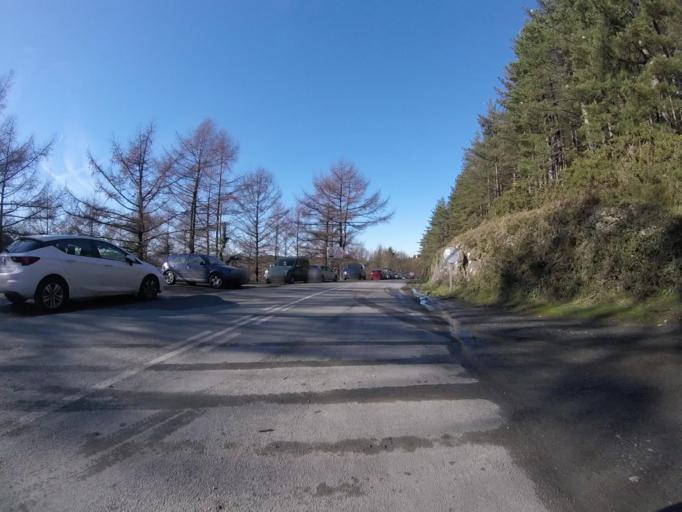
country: ES
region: Basque Country
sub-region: Provincia de Guipuzcoa
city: Irun
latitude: 43.2953
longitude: -1.7867
